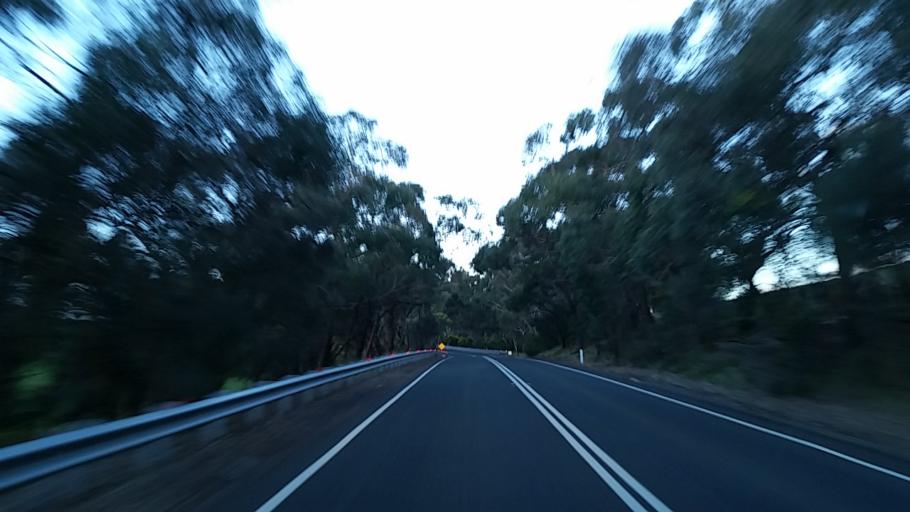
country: AU
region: South Australia
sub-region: Barossa
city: Williamstown
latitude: -34.7217
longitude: 138.8781
